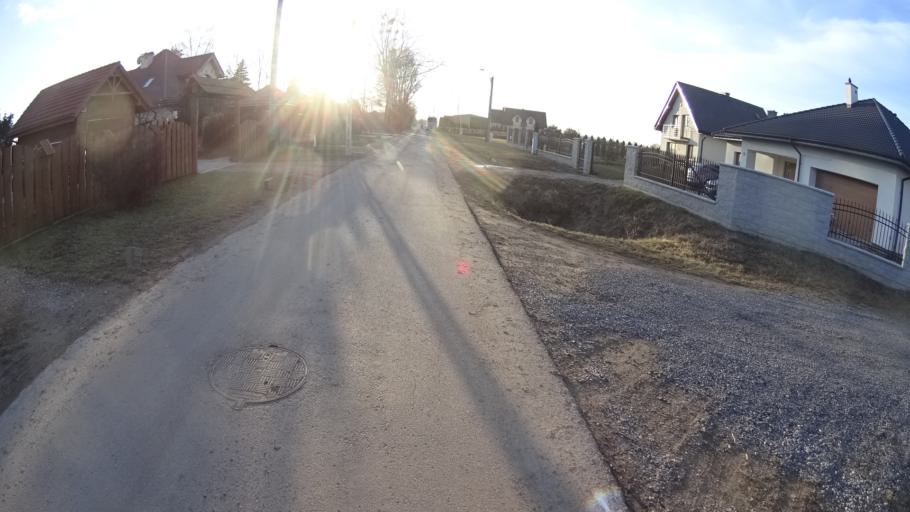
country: PL
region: Masovian Voivodeship
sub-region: Powiat warszawski zachodni
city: Truskaw
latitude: 52.2529
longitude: 20.7537
